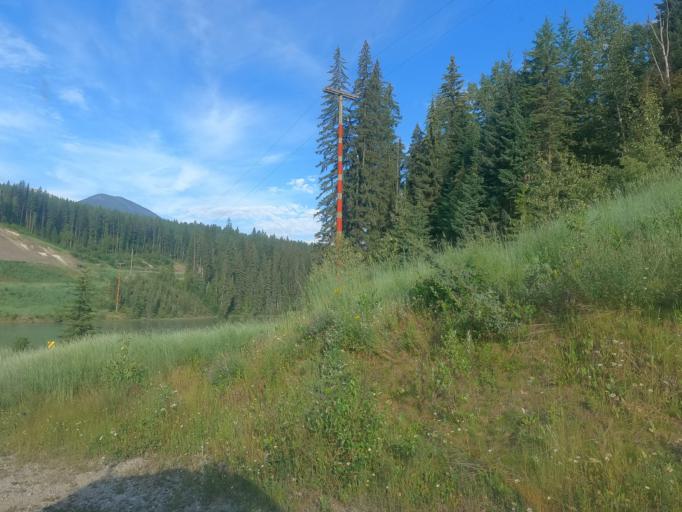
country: CA
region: British Columbia
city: Golden
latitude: 51.4854
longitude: -117.1806
